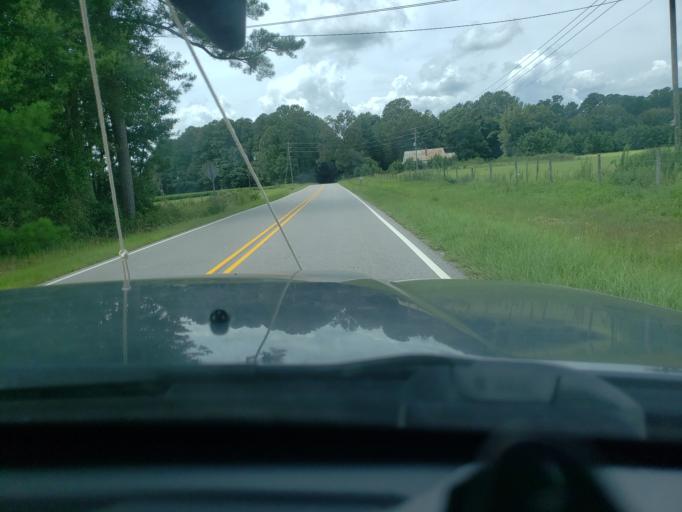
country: US
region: North Carolina
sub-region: Wake County
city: Rolesville
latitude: 35.8826
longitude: -78.4013
